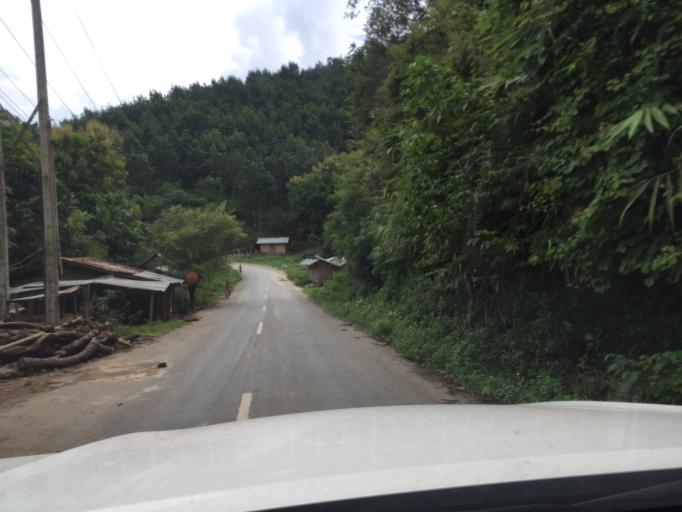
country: LA
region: Oudomxai
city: Muang La
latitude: 21.1096
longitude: 102.2022
